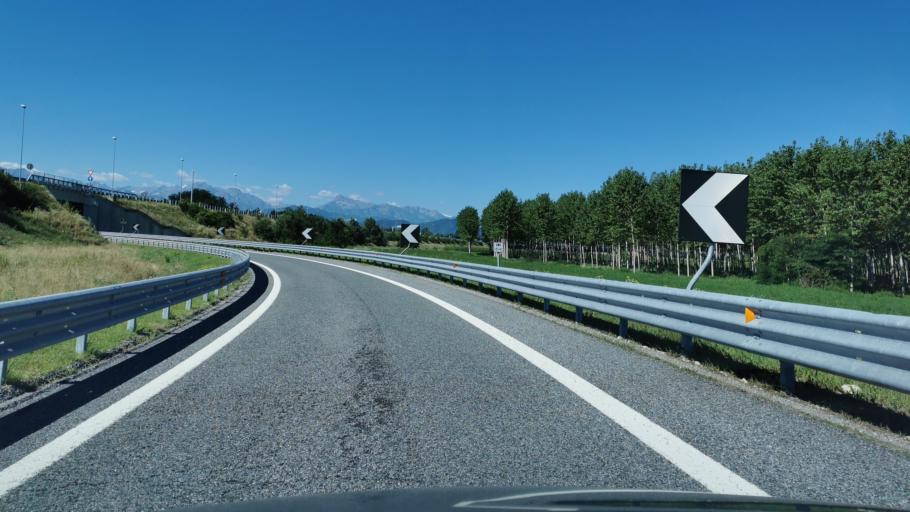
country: IT
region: Piedmont
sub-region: Provincia di Cuneo
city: Castelletto Stura
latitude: 44.4254
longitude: 7.5900
